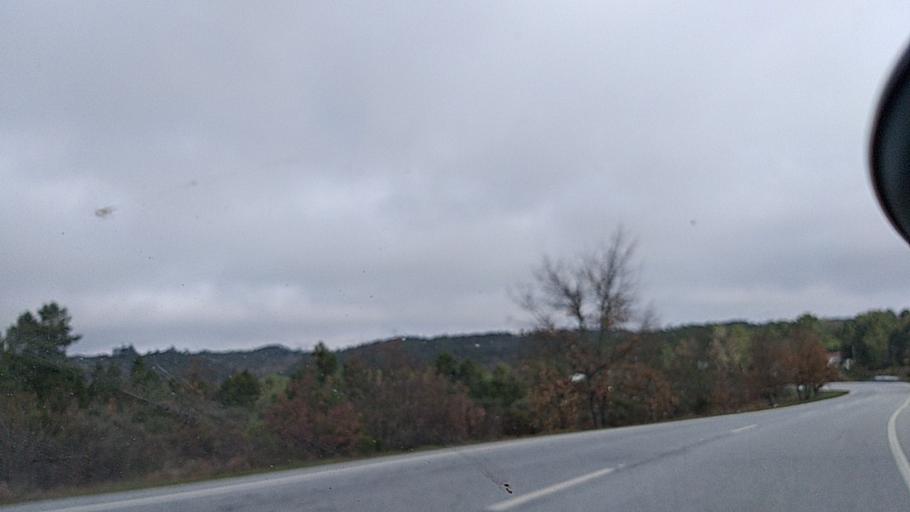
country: PT
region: Guarda
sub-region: Aguiar da Beira
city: Aguiar da Beira
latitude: 40.7761
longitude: -7.5056
